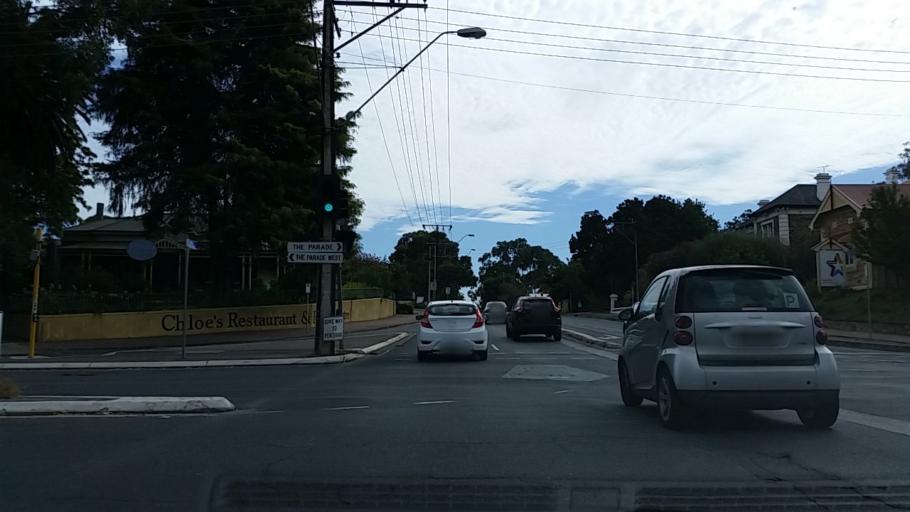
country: AU
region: South Australia
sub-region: Norwood Payneham St Peters
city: Trinity Gardens
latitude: -34.9218
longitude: 138.6231
